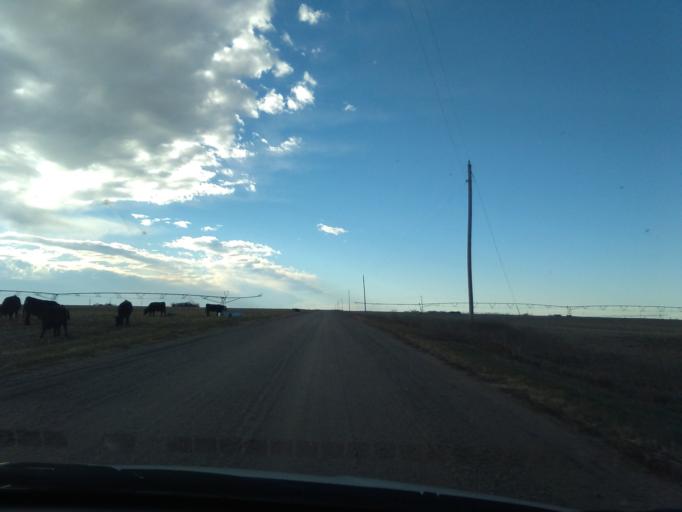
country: US
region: Nebraska
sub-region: Kearney County
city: Minden
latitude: 40.3649
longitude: -98.8209
